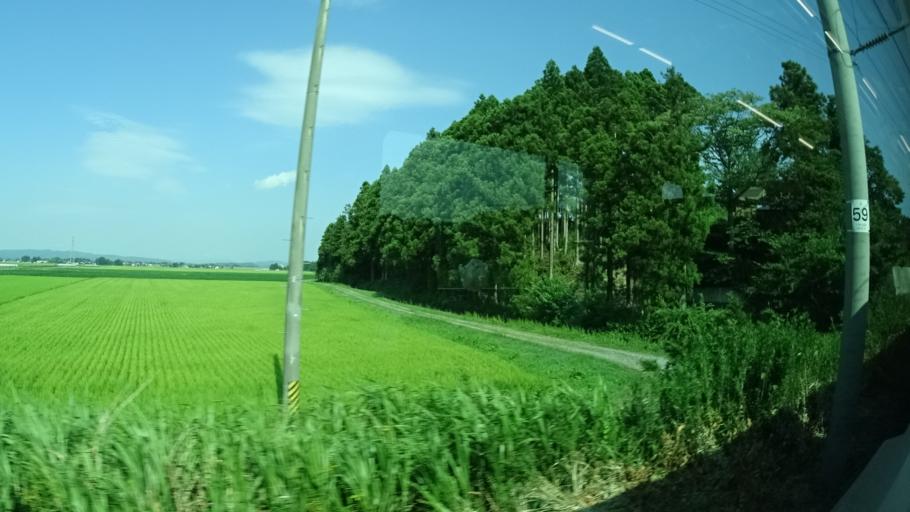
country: JP
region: Miyagi
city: Kogota
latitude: 38.5004
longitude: 141.0841
